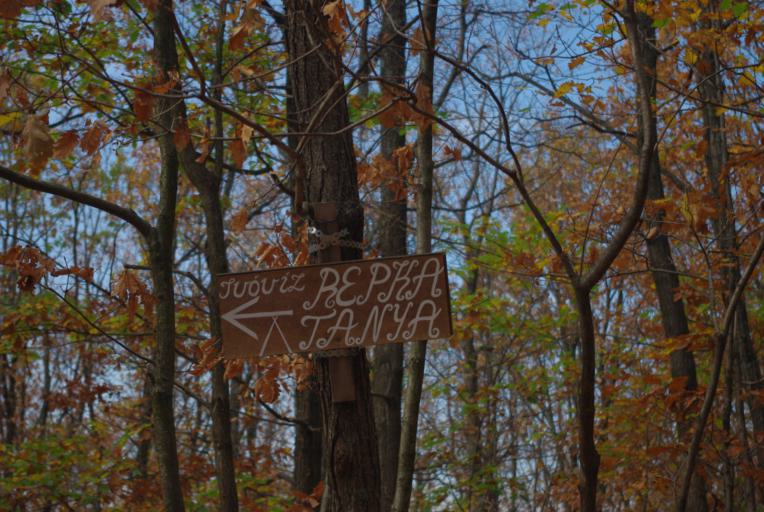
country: HU
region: Borsod-Abauj-Zemplen
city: Sarospatak
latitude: 48.3892
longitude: 21.5793
